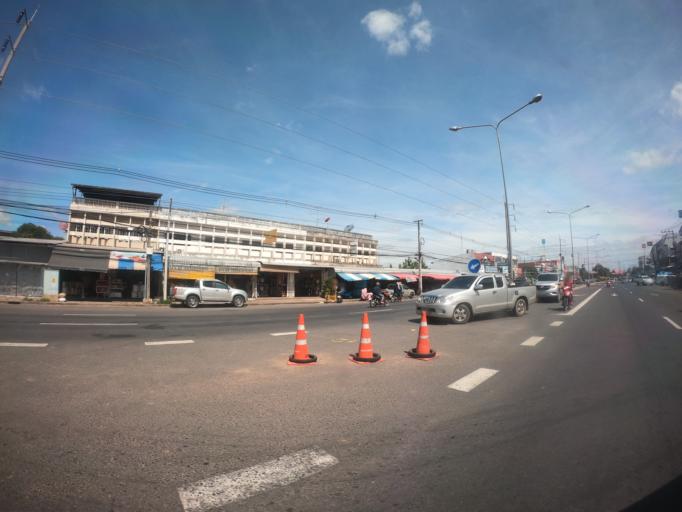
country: TH
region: Surin
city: Prasat
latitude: 14.6365
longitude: 103.4066
